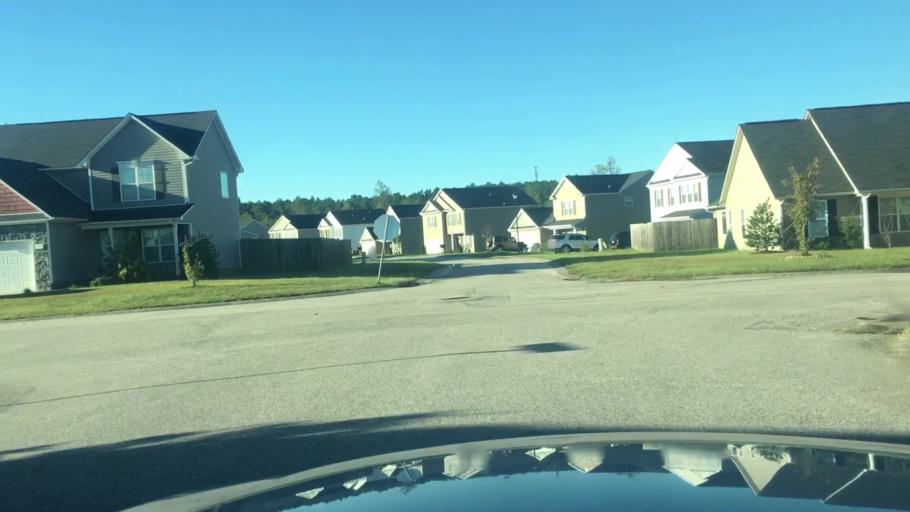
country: US
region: North Carolina
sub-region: Harnett County
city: Lillington
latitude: 35.3438
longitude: -78.8516
